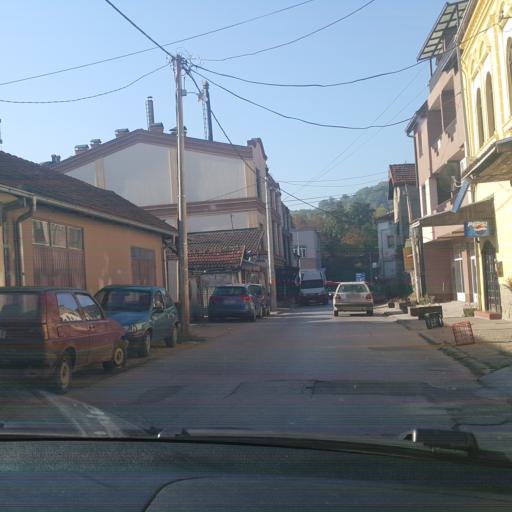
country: RS
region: Central Serbia
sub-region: Toplicki Okrug
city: Prokuplje
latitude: 43.2326
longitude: 21.5837
